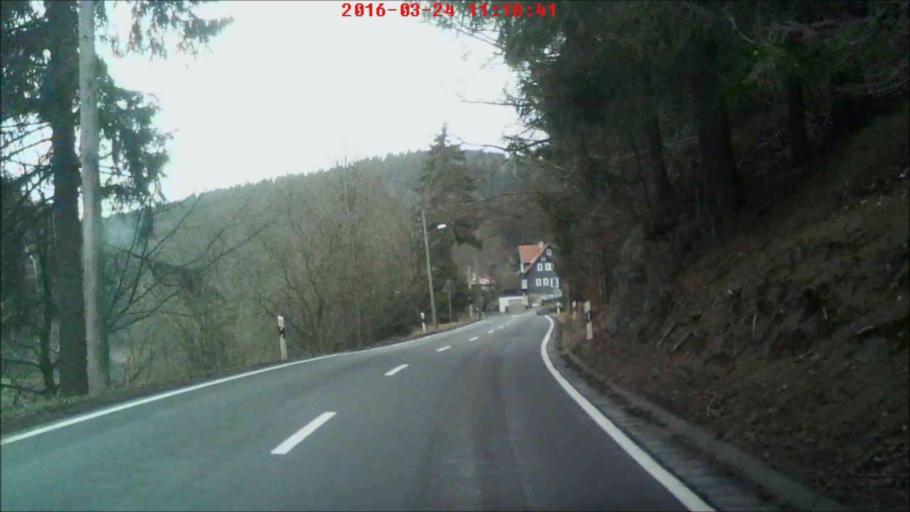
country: DE
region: Thuringia
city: Masserberg
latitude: 50.4961
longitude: 10.9259
